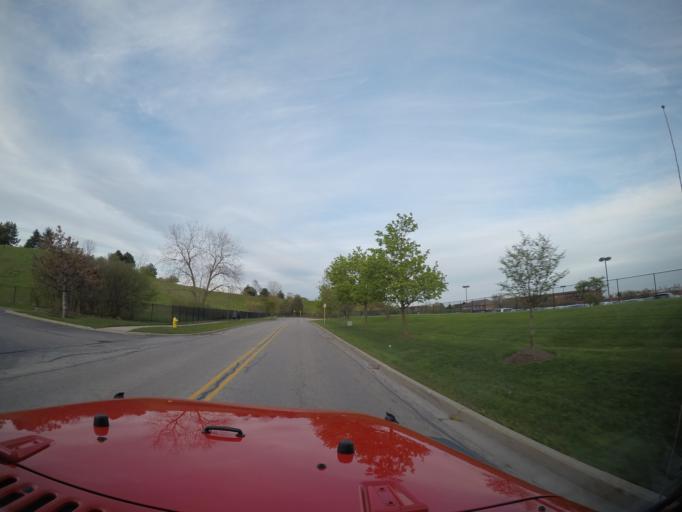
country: US
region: Illinois
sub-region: Cook County
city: Glenview
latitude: 42.0900
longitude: -87.8116
